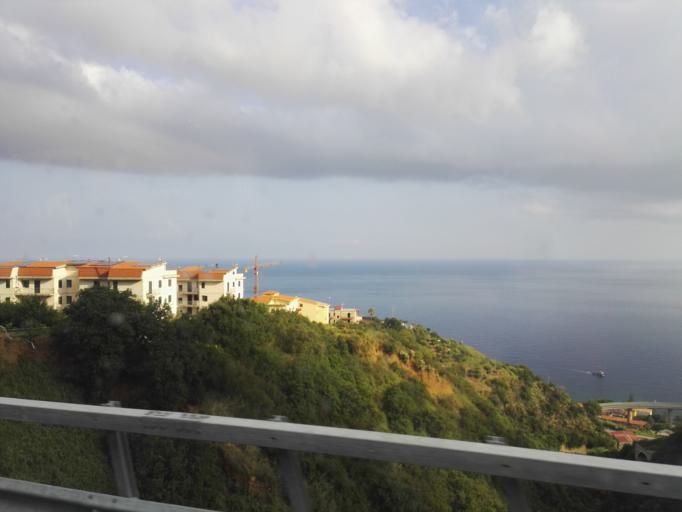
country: IT
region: Calabria
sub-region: Provincia di Reggio Calabria
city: Scilla
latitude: 38.2487
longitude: 15.7267
